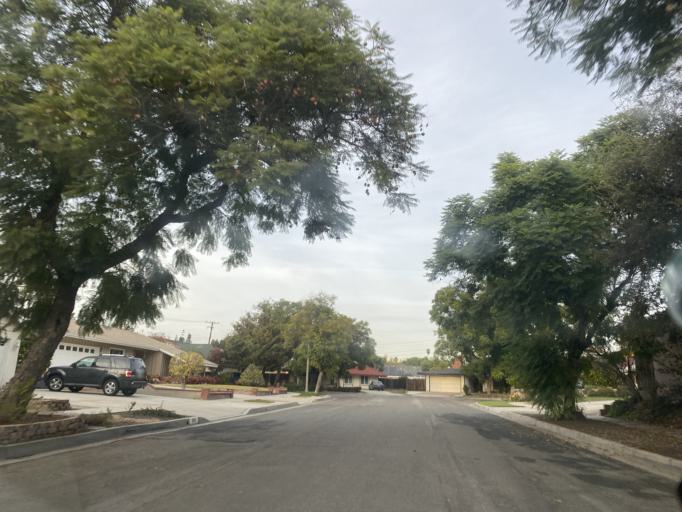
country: US
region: California
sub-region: Orange County
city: Placentia
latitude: 33.8937
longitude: -117.8817
